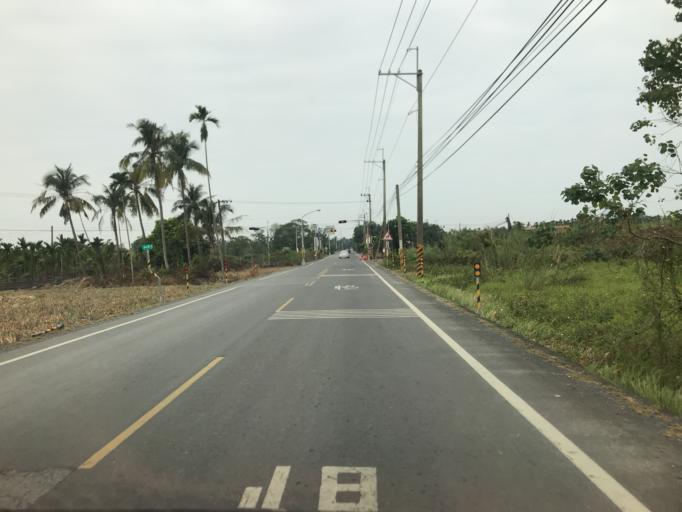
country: TW
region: Taiwan
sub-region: Pingtung
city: Pingtung
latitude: 22.4711
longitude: 120.6080
